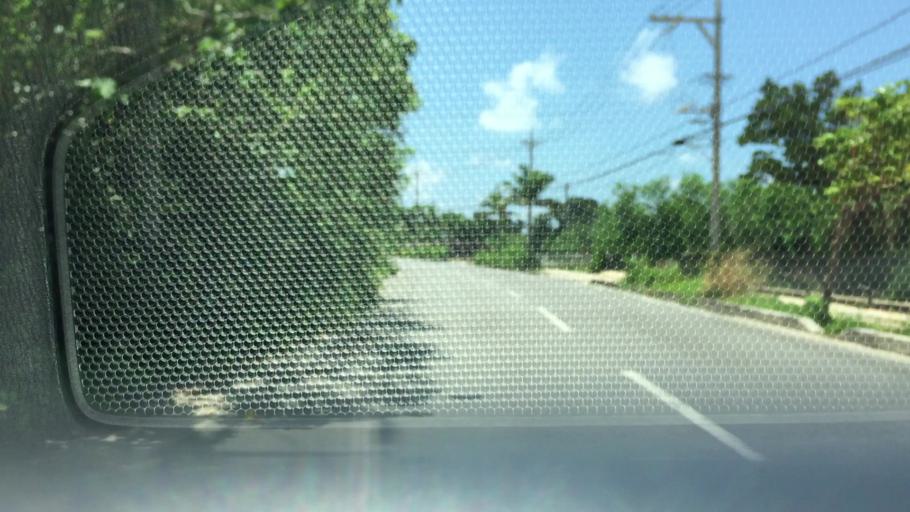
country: JP
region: Okinawa
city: Ishigaki
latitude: 24.3613
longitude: 124.1189
